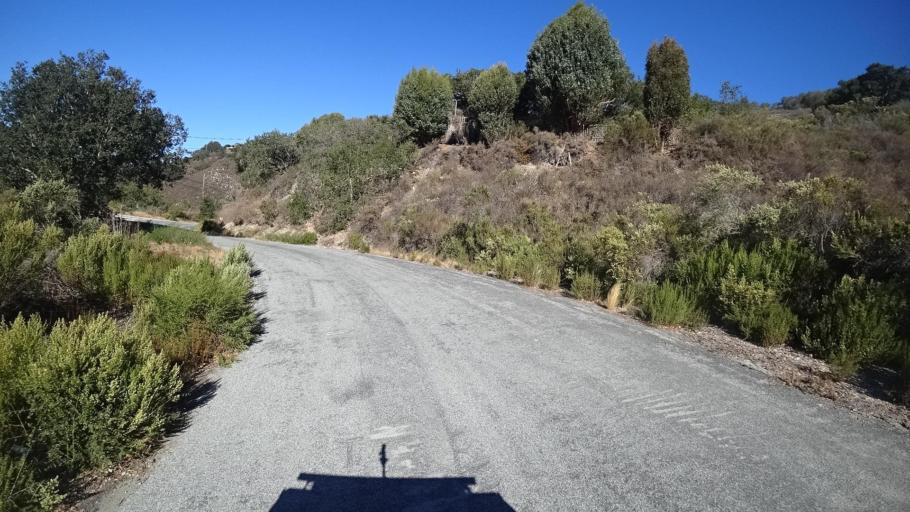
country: US
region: California
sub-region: Monterey County
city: Carmel Valley Village
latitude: 36.5147
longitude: -121.7707
